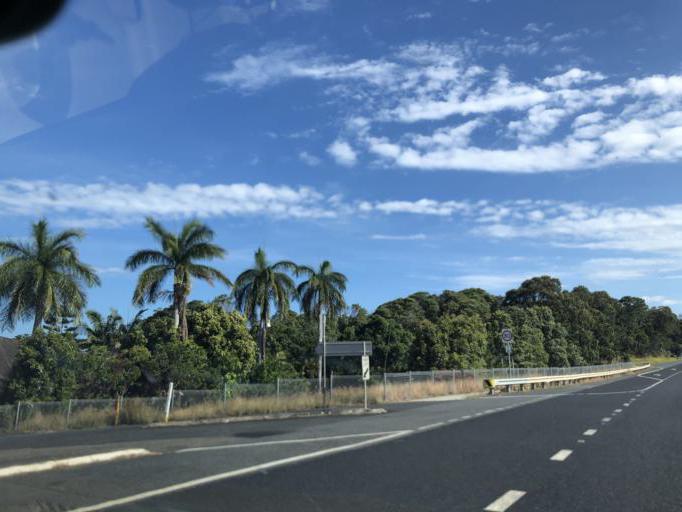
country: AU
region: New South Wales
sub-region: Coffs Harbour
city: Moonee Beach
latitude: -30.2392
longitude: 153.1468
